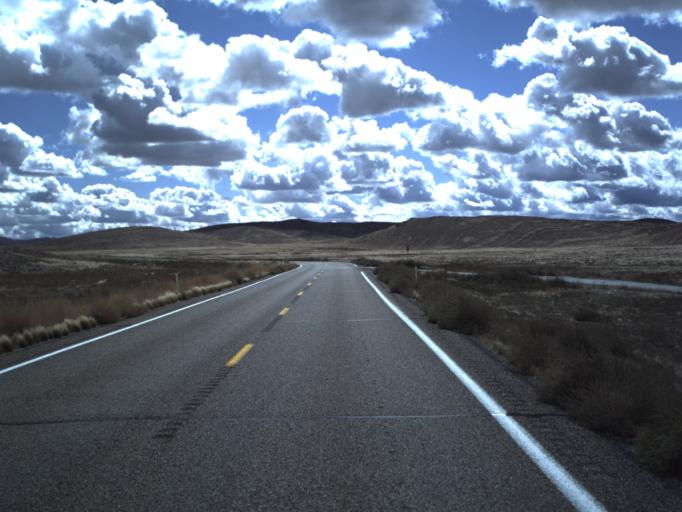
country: US
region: Nevada
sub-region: Lincoln County
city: Pioche
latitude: 38.7300
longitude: -113.9370
